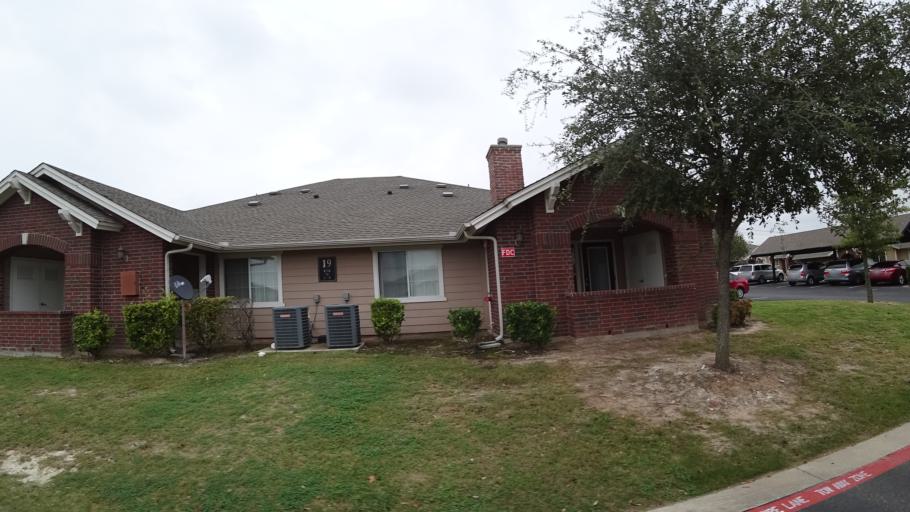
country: US
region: Texas
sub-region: Travis County
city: Pflugerville
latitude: 30.4297
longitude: -97.6203
